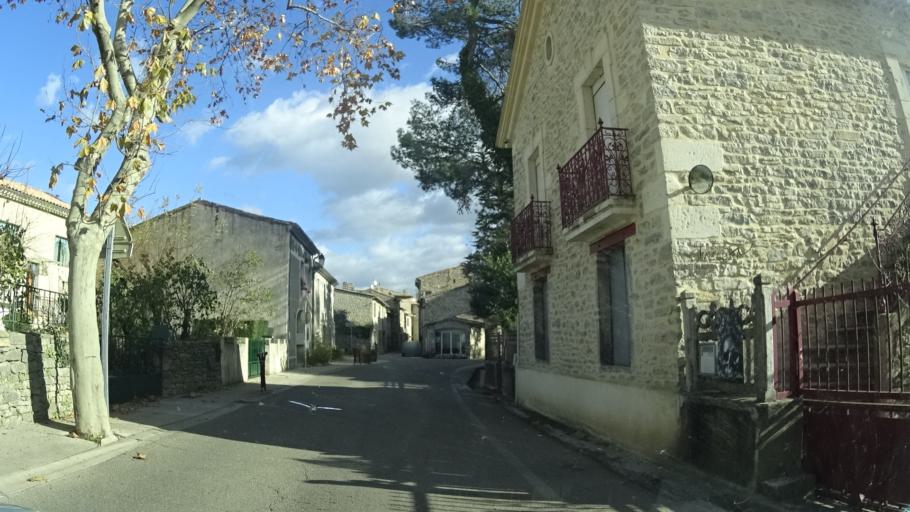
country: FR
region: Languedoc-Roussillon
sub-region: Departement de l'Herault
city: Claret
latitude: 43.8619
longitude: 3.9043
